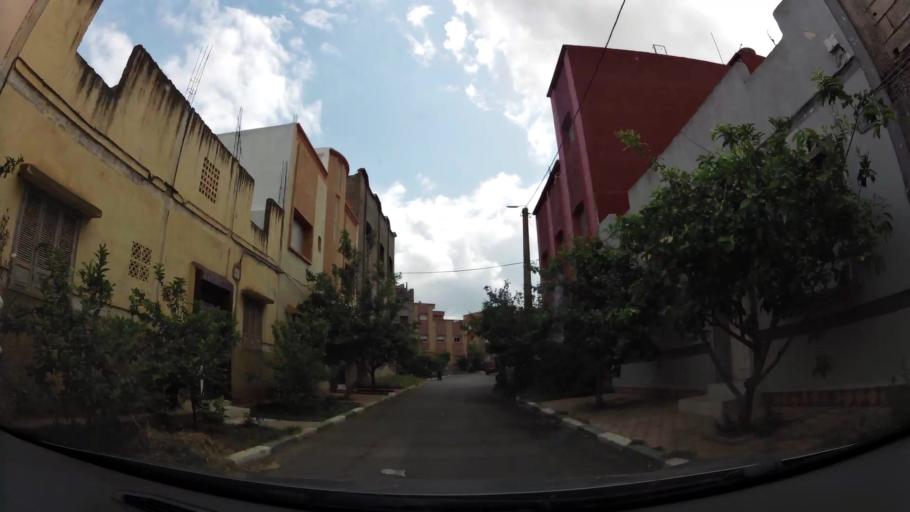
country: MA
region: Rabat-Sale-Zemmour-Zaer
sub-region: Khemisset
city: Tiflet
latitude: 33.8876
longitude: -6.3314
